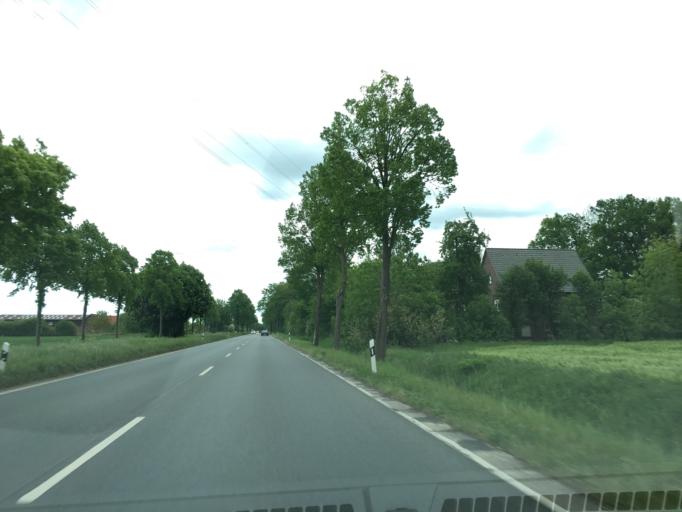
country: DE
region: North Rhine-Westphalia
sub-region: Regierungsbezirk Munster
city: Drensteinfurt
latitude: 51.8393
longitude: 7.6769
